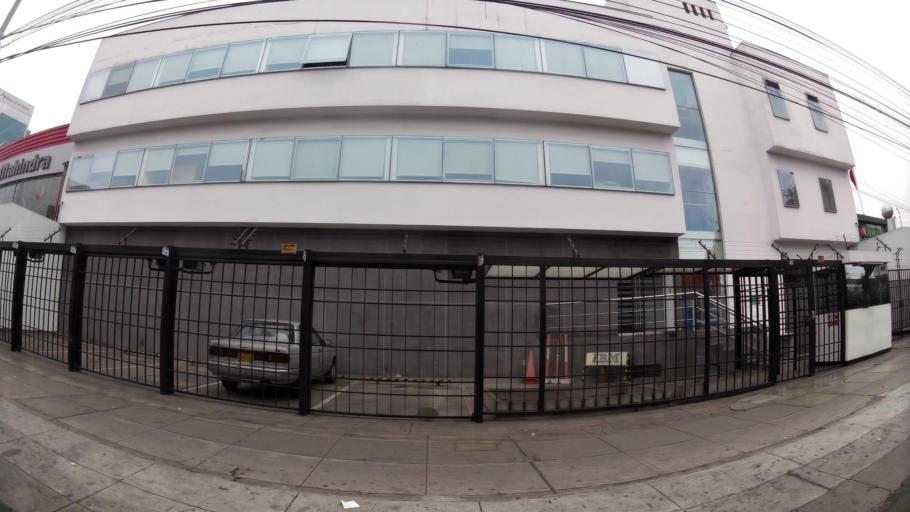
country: PE
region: Lima
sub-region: Lima
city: San Luis
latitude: -12.1020
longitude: -77.0181
